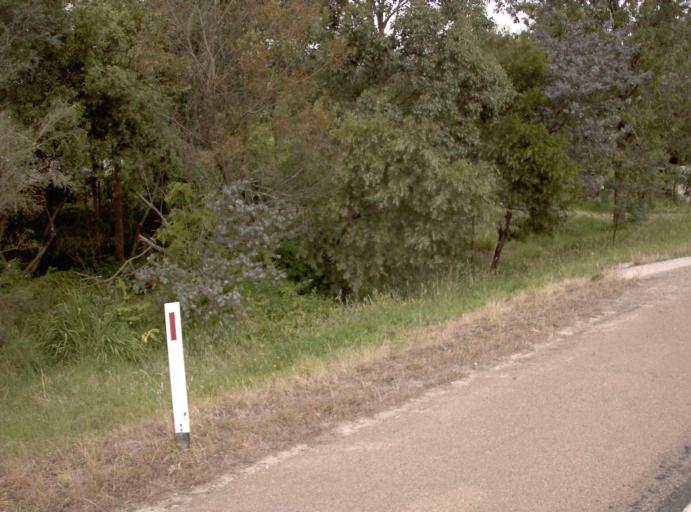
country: AU
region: Victoria
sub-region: East Gippsland
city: Lakes Entrance
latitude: -37.7292
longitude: 148.0891
